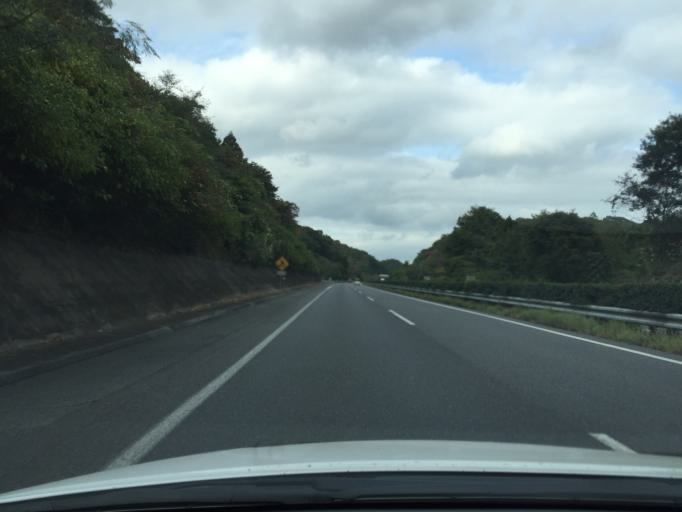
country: JP
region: Fukushima
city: Iwaki
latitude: 36.9580
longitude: 140.7807
